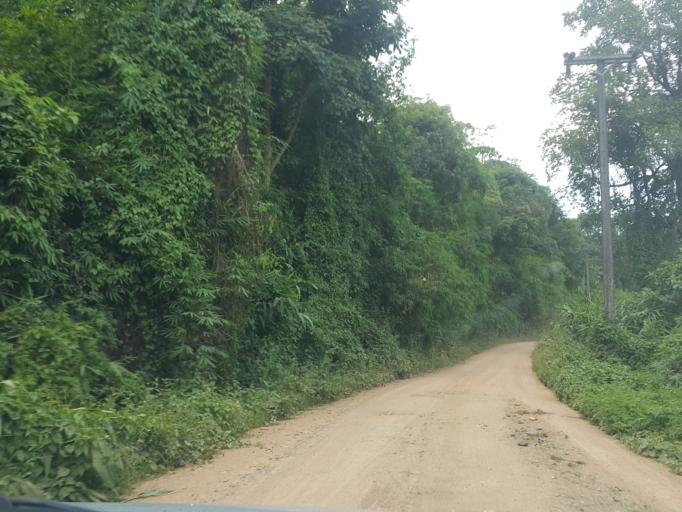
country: TH
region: Chiang Mai
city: Phrao
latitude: 19.3287
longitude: 99.1394
